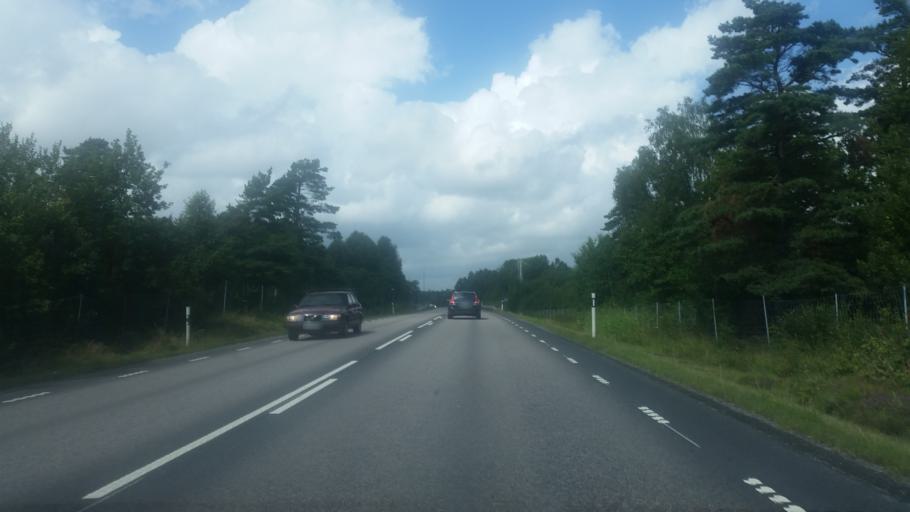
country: SE
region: Vaestra Goetaland
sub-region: Partille Kommun
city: Furulund
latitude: 57.7161
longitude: 12.1418
